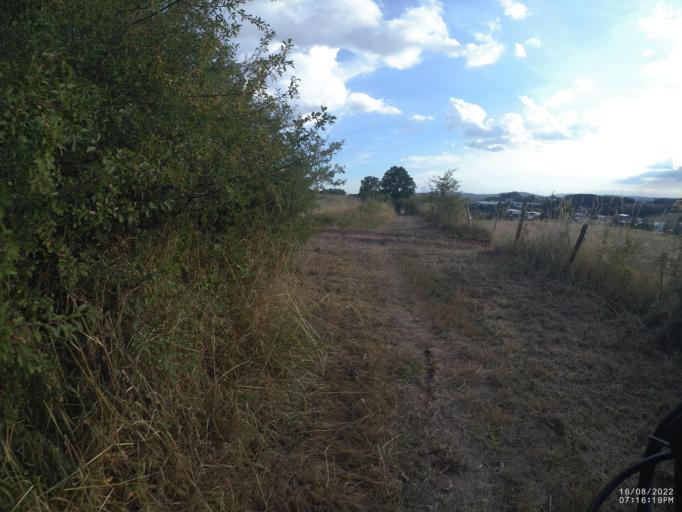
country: DE
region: Rheinland-Pfalz
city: Hillesheim
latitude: 50.3005
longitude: 6.6775
